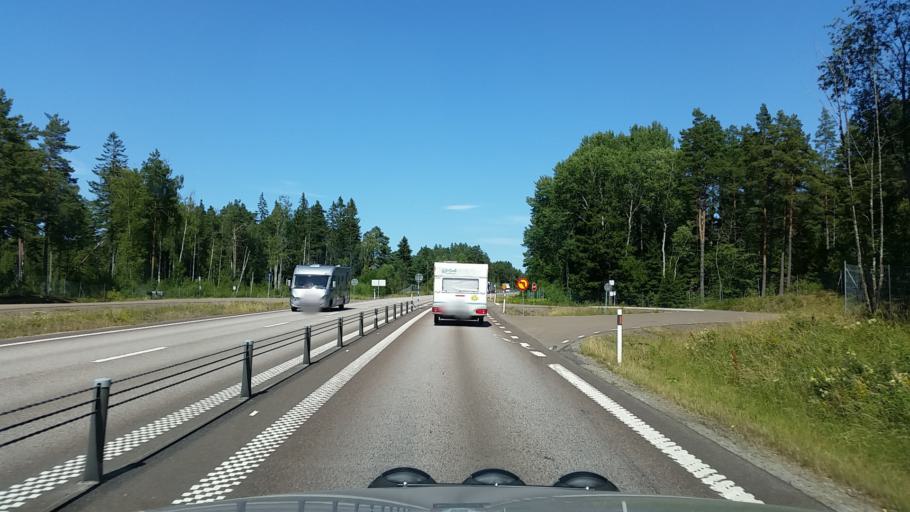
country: SE
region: Vaestra Goetaland
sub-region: Melleruds Kommun
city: Mellerud
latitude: 58.8245
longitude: 12.5252
